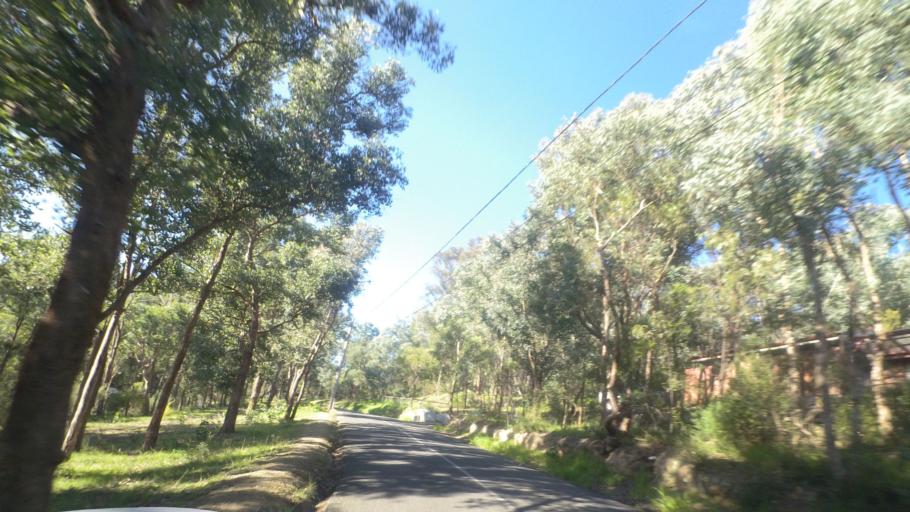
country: AU
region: Victoria
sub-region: Nillumbik
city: North Warrandyte
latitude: -37.7200
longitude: 145.2197
